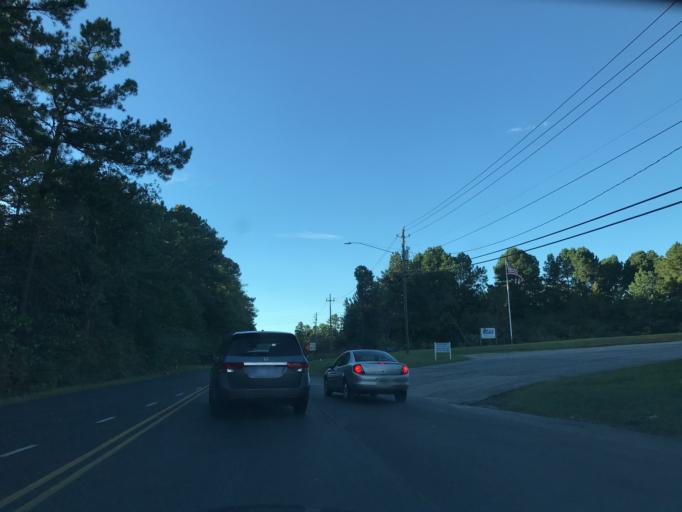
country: US
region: North Carolina
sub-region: Wake County
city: Morrisville
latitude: 35.8406
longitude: -78.8323
